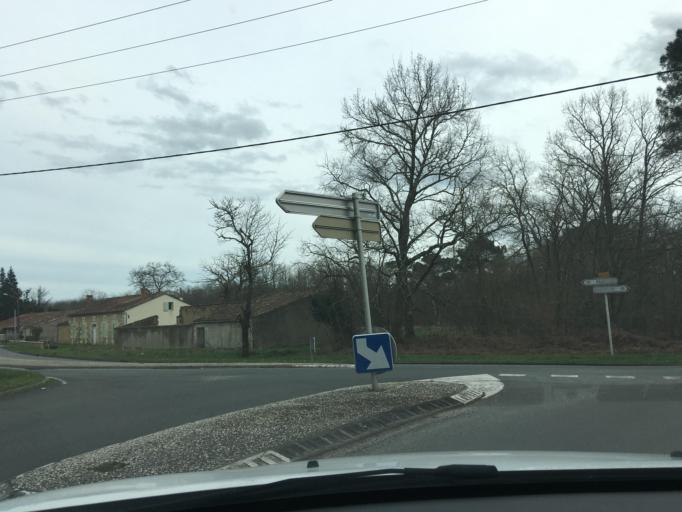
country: FR
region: Aquitaine
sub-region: Departement de la Gironde
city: Saint-Sauveur
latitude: 45.2196
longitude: -0.8691
